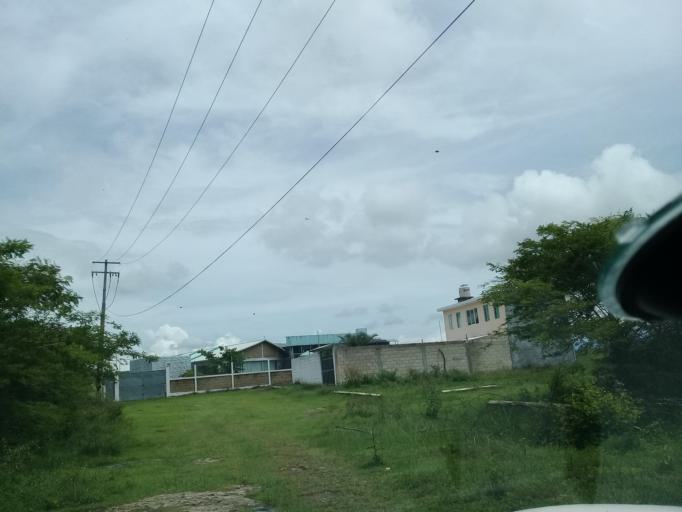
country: MX
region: Veracruz
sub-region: Emiliano Zapata
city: Dos Rios
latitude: 19.4704
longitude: -96.7771
